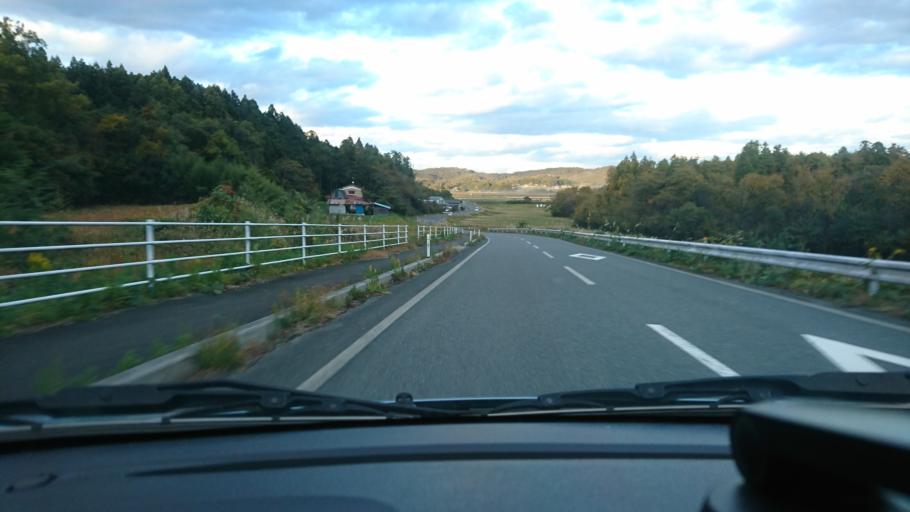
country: JP
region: Iwate
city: Ichinoseki
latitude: 38.8091
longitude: 141.1953
